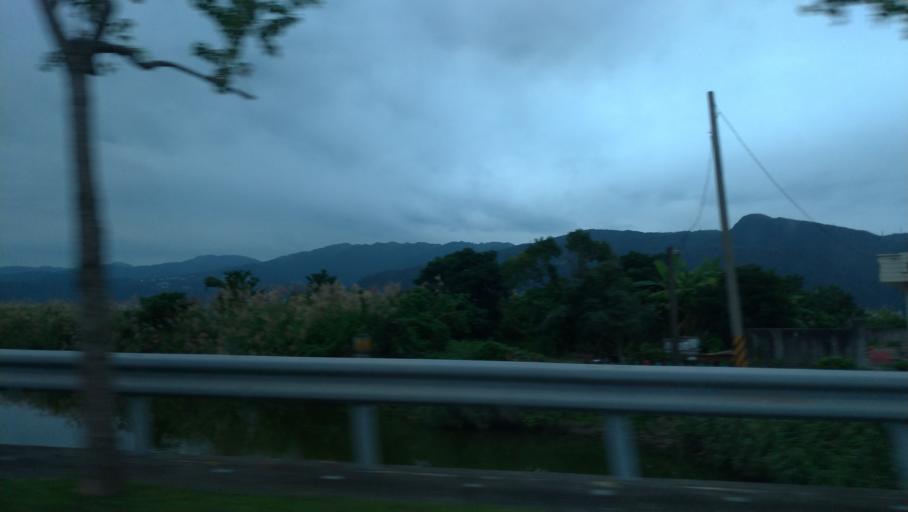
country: TW
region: Taiwan
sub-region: Yilan
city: Yilan
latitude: 24.8242
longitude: 121.7994
